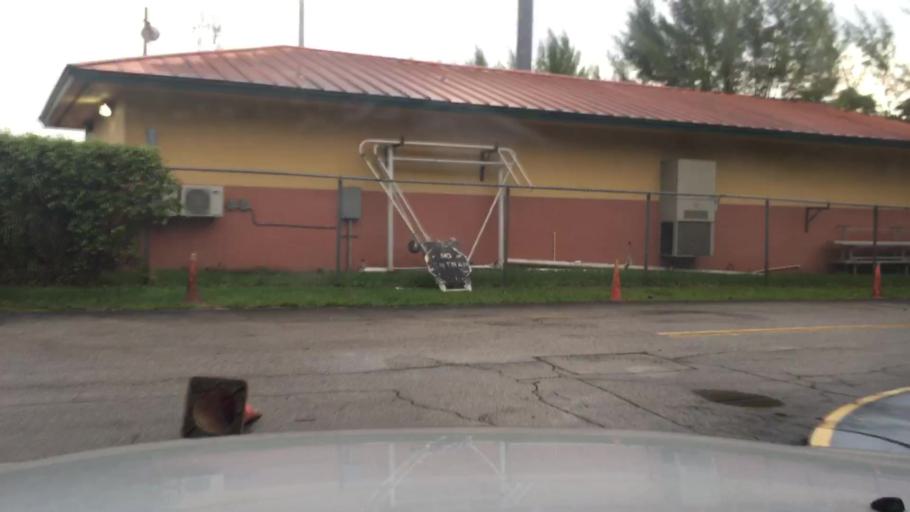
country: US
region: Florida
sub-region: Miami-Dade County
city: Hialeah
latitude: 25.8643
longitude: -80.2850
